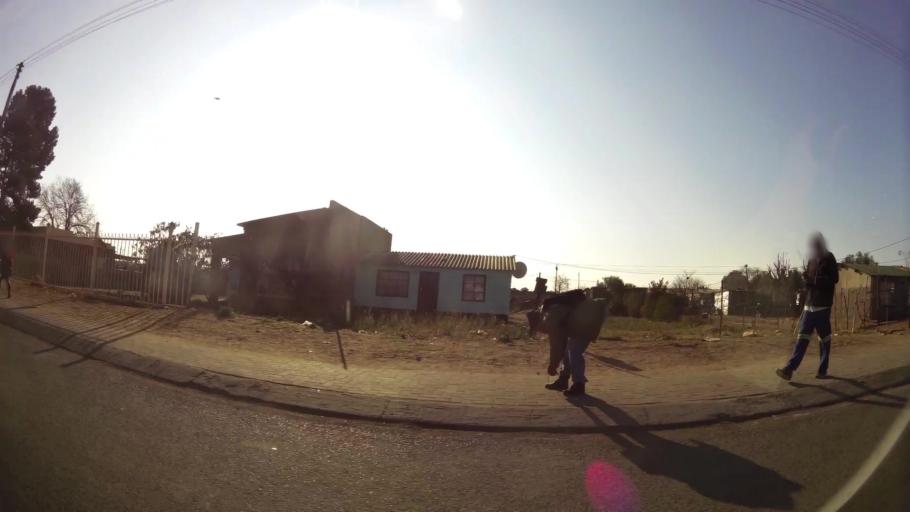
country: ZA
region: Orange Free State
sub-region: Mangaung Metropolitan Municipality
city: Bloemfontein
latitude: -29.1506
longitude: 26.2516
